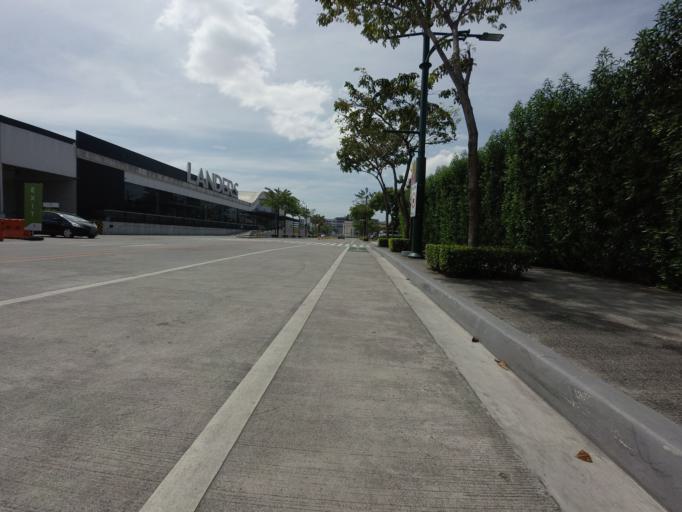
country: PH
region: Metro Manila
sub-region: Pasig
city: Pasig City
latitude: 14.5793
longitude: 121.0772
